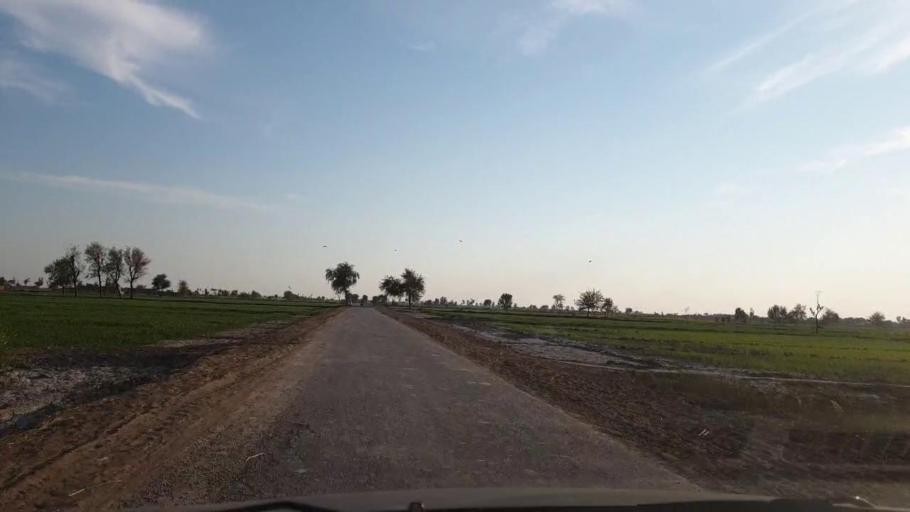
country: PK
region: Sindh
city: Khadro
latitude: 26.1680
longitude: 68.7532
